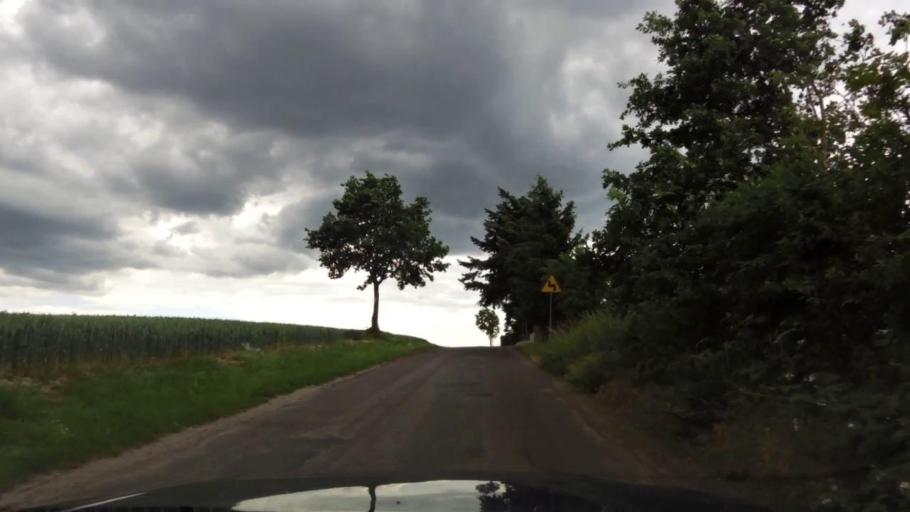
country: PL
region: West Pomeranian Voivodeship
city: Trzcinsko Zdroj
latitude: 52.9225
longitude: 14.5923
